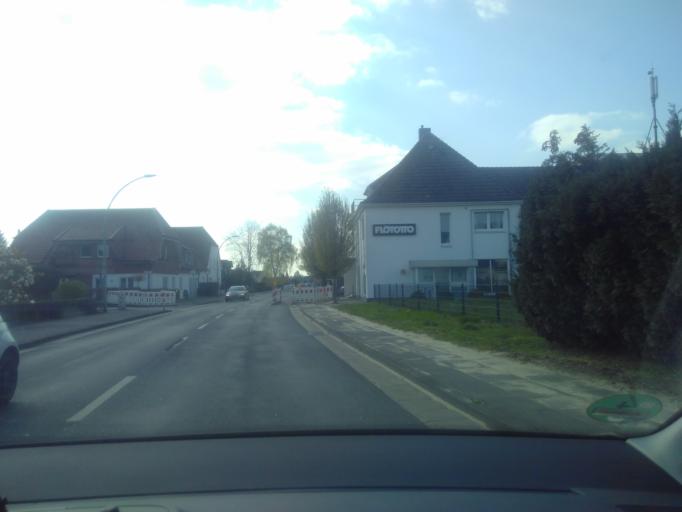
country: DE
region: North Rhine-Westphalia
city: Rietberg
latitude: 51.8595
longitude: 8.4365
